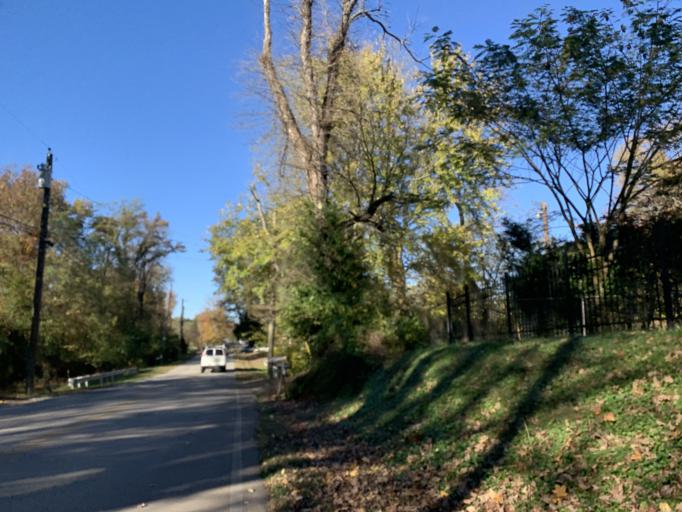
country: US
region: Kentucky
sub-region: Jefferson County
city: Pleasure Ridge Park
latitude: 38.1515
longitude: -85.8774
